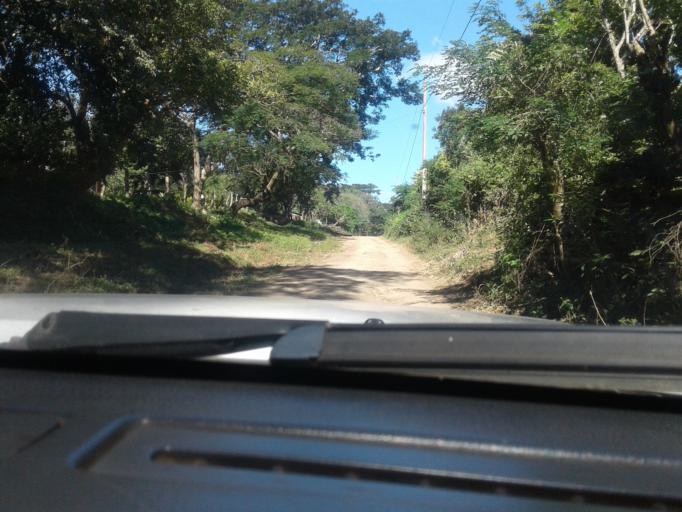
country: NI
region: Carazo
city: Santa Teresa
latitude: 11.7909
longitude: -86.1810
